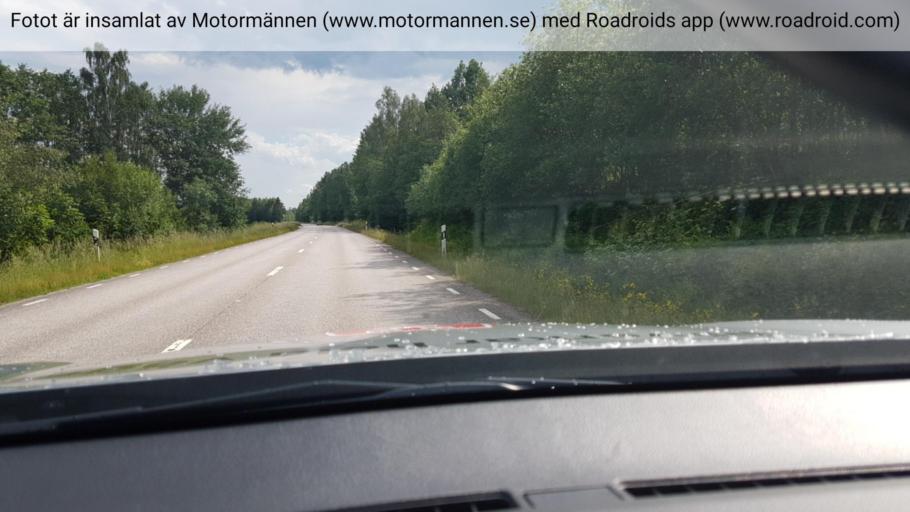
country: SE
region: Vaestra Goetaland
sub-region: Hjo Kommun
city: Hjo
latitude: 58.2095
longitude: 14.2049
